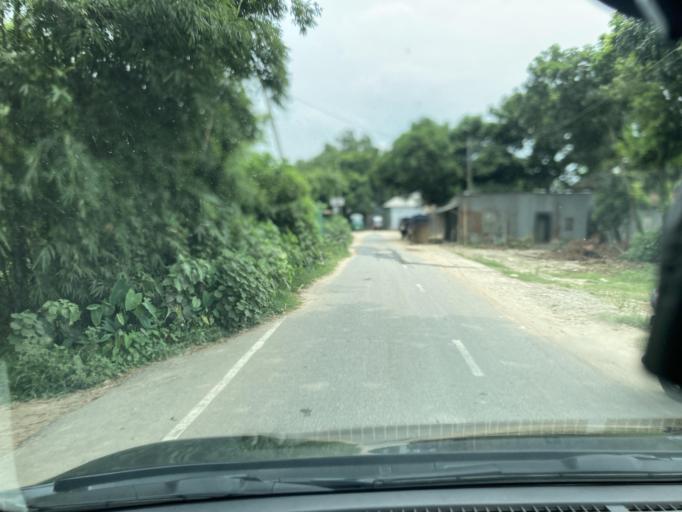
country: BD
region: Dhaka
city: Dohar
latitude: 23.7702
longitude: 90.0673
